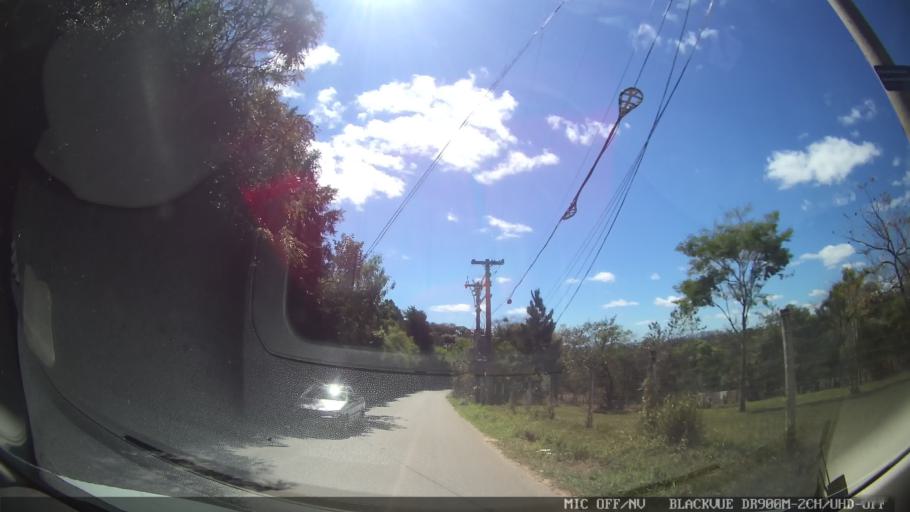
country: BR
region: Sao Paulo
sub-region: Campo Limpo Paulista
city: Campo Limpo Paulista
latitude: -23.1766
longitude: -46.7412
